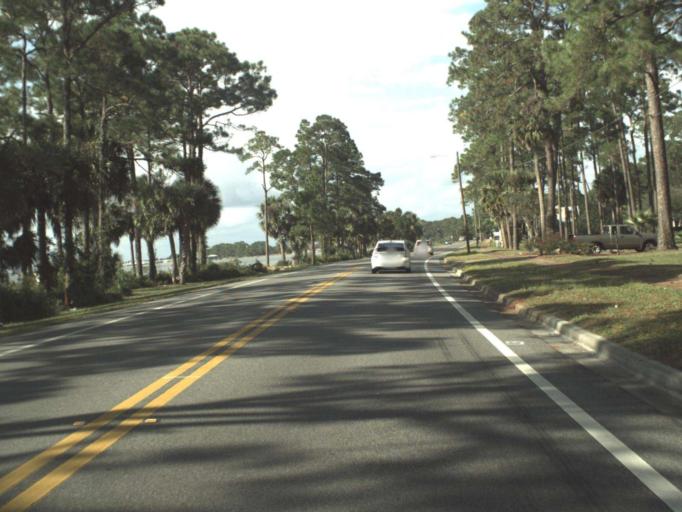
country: US
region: Florida
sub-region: Gulf County
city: Port Saint Joe
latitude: 29.8005
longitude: -85.3010
